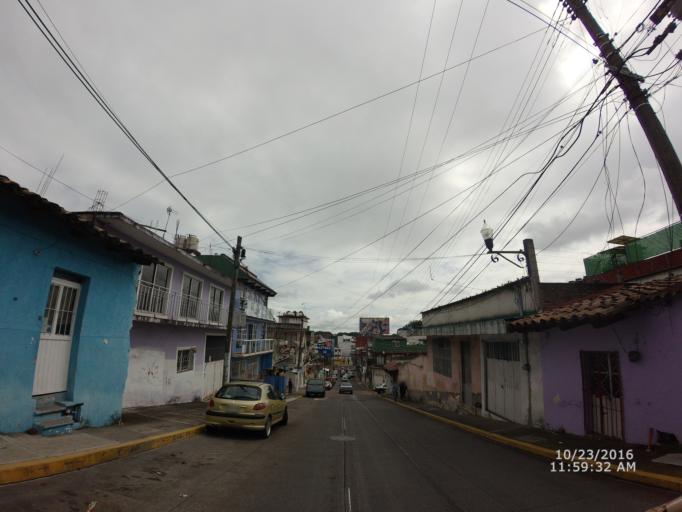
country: MX
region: Veracruz
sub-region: Xalapa
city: Xalapa de Enriquez
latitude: 19.5330
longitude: -96.9168
